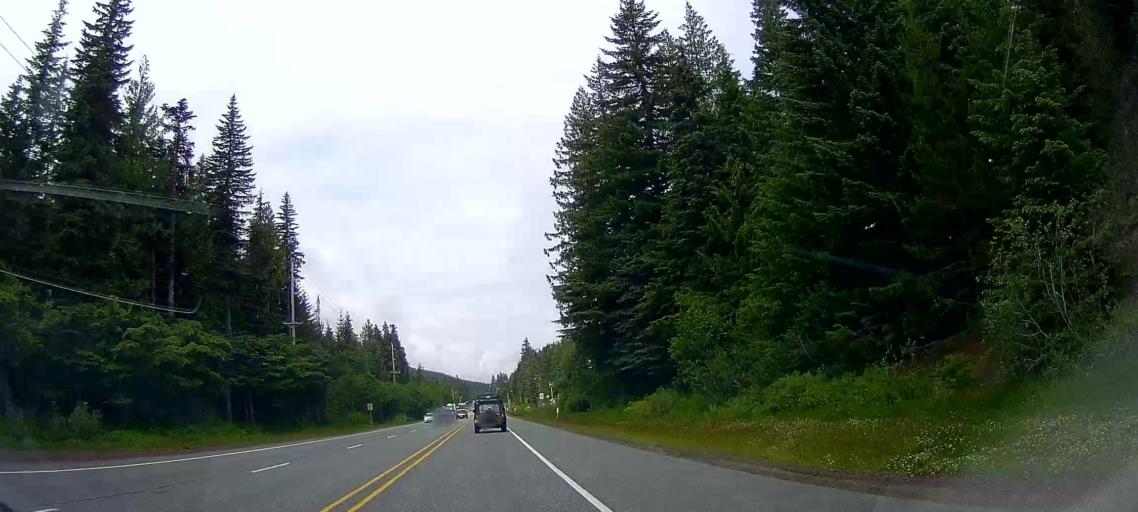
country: US
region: Oregon
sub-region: Clackamas County
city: Mount Hood Village
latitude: 45.3026
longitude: -121.7637
